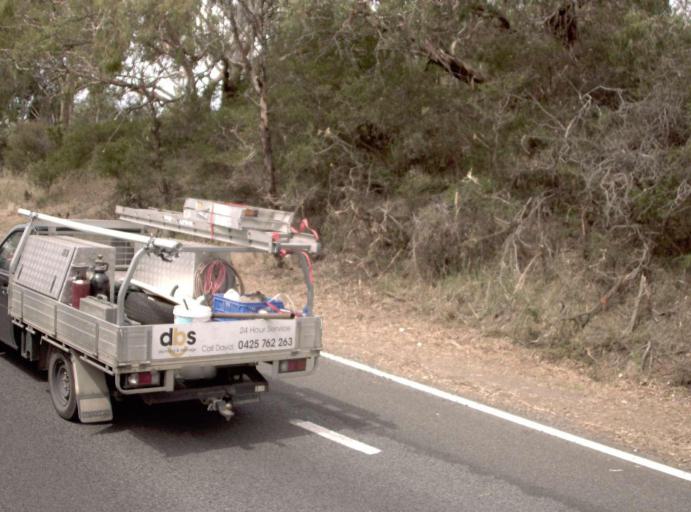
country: AU
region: Victoria
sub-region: Mornington Peninsula
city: Moorooduc
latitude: -38.2498
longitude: 145.0815
